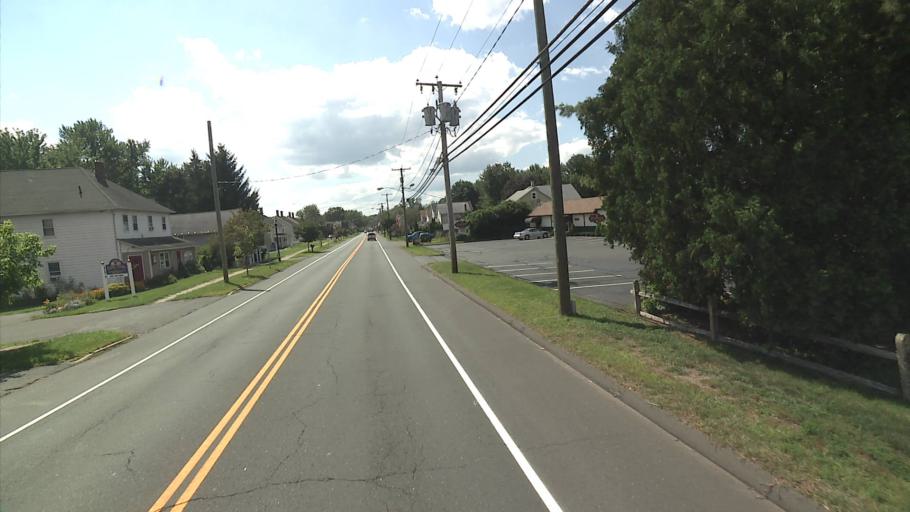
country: US
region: Connecticut
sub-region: Tolland County
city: Somers
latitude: 41.9858
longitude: -72.4859
